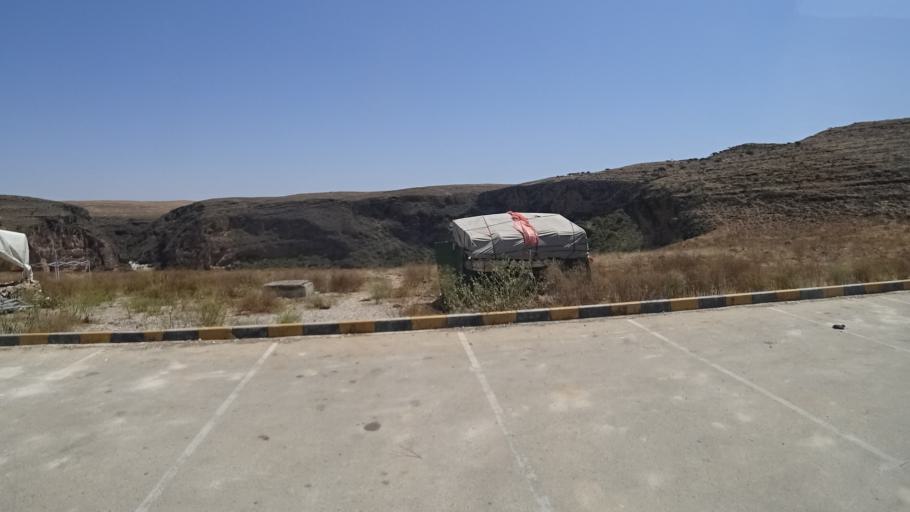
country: OM
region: Zufar
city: Salalah
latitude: 17.1538
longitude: 54.6224
